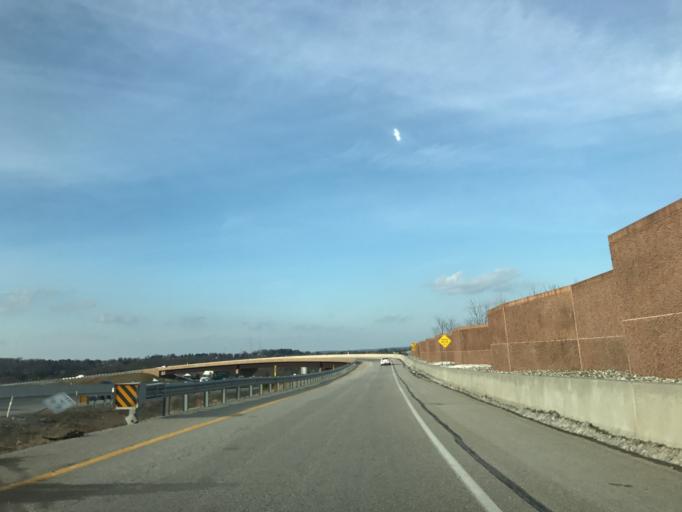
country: US
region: Pennsylvania
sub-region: York County
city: Spry
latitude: 39.9169
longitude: -76.7043
